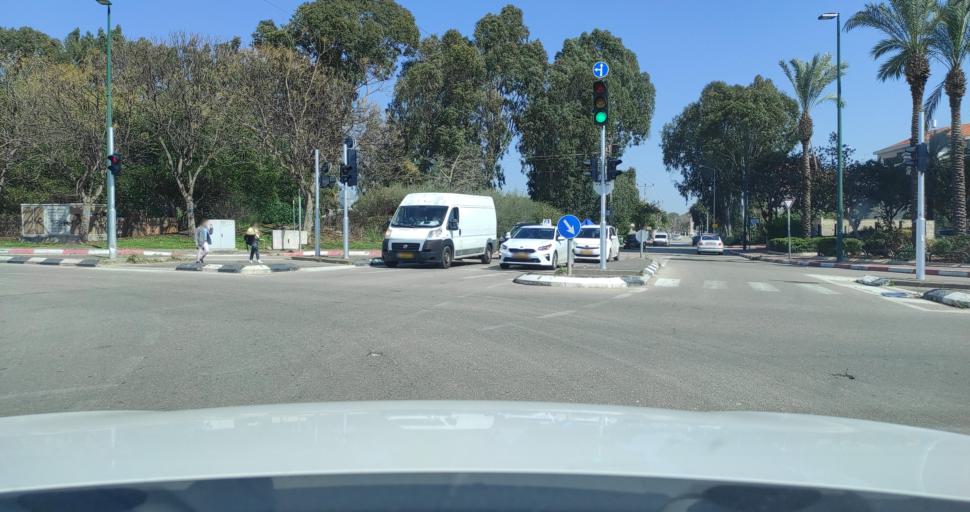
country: IL
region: Central District
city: Nordiyya
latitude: 32.3110
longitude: 34.8760
